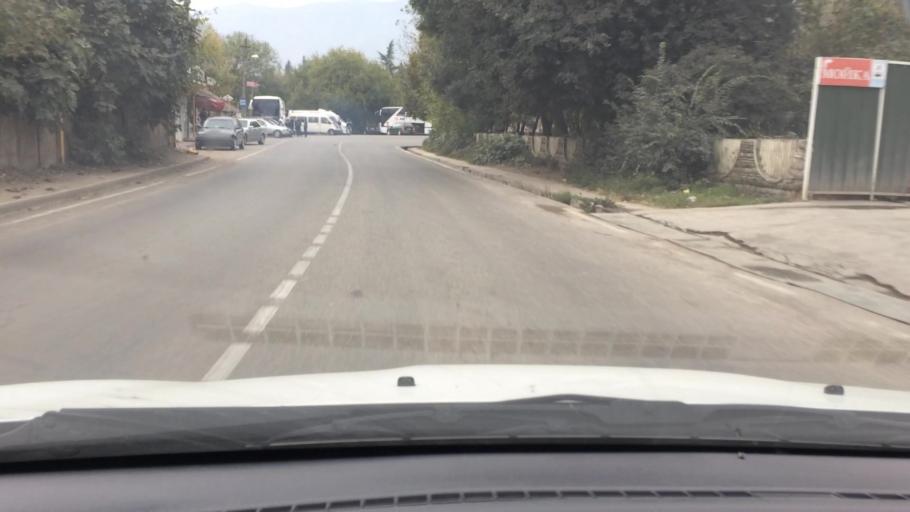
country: AM
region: Tavush
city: Bagratashen
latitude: 41.2470
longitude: 44.7990
